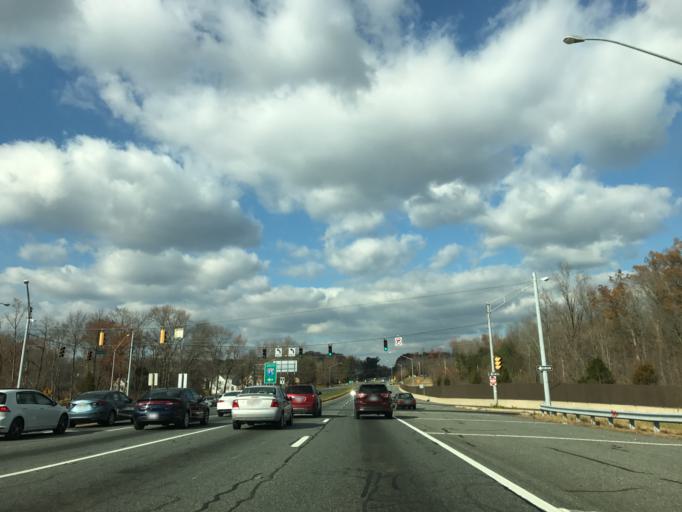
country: US
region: Maryland
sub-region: Harford County
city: Joppatowne
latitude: 39.4425
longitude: -76.3488
